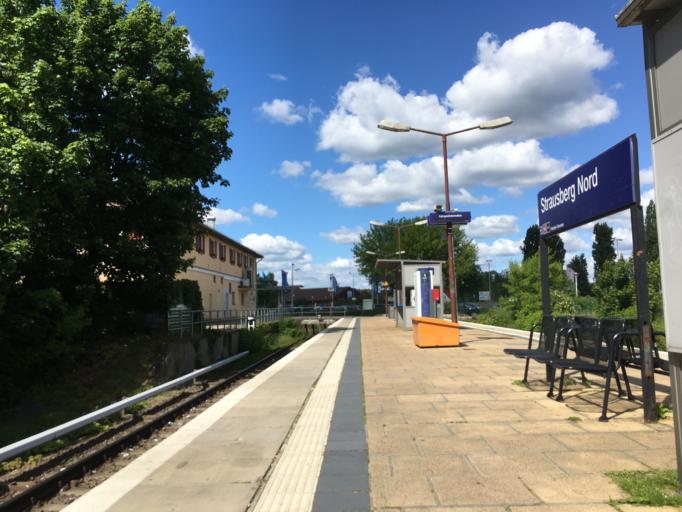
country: DE
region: Brandenburg
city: Strausberg
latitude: 52.5905
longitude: 13.9086
